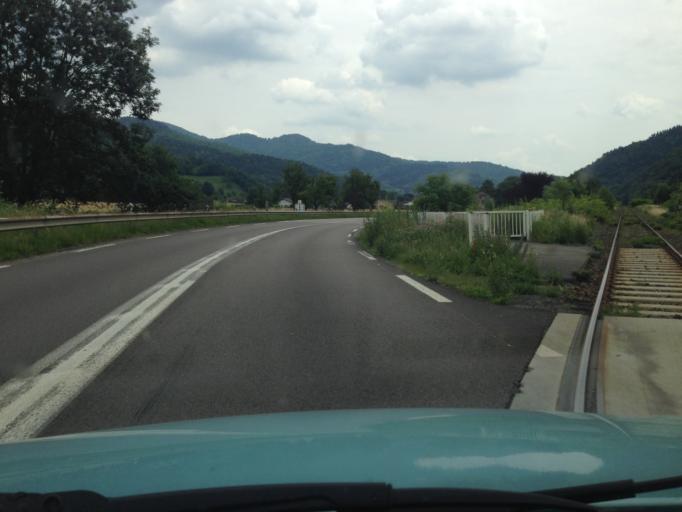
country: FR
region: Alsace
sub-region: Departement du Haut-Rhin
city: Moosch
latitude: 47.8527
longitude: 7.0596
